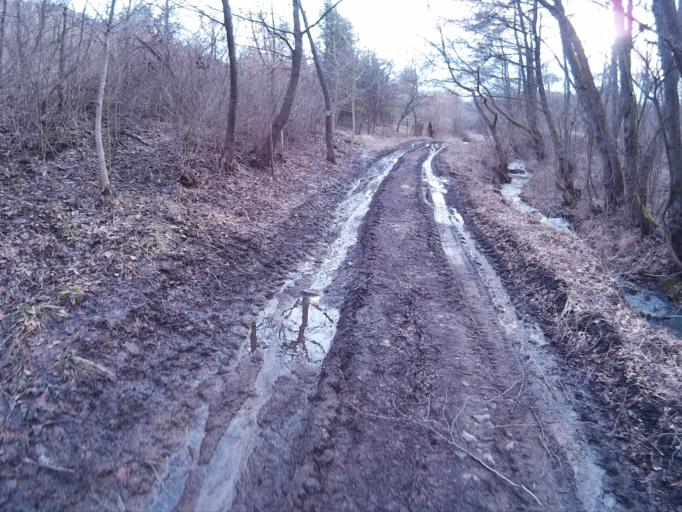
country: HU
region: Borsod-Abauj-Zemplen
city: Gonc
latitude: 48.3966
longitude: 21.3479
